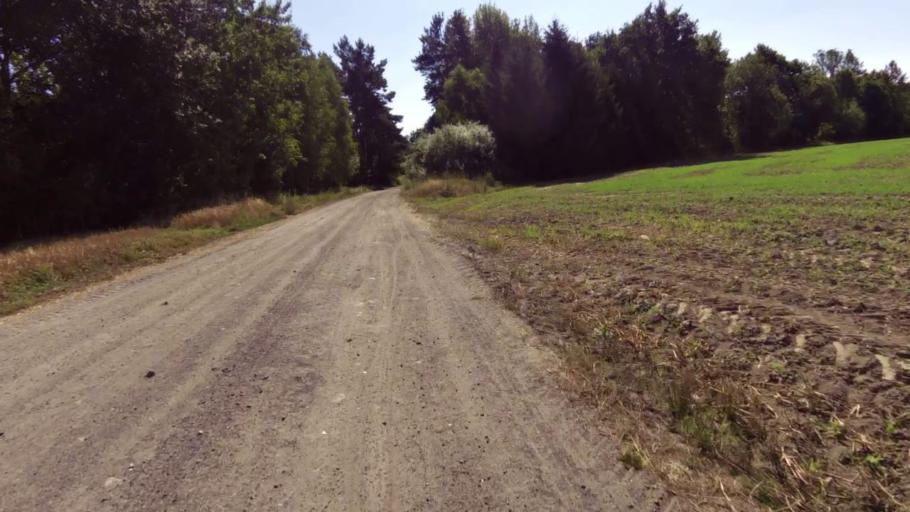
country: PL
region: West Pomeranian Voivodeship
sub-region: Powiat drawski
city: Zlocieniec
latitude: 53.5229
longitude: 16.0445
